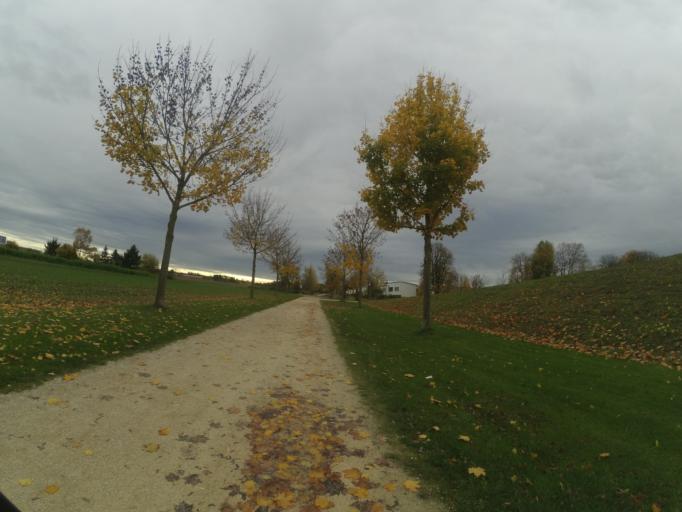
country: DE
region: Bavaria
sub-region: Swabia
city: Neu-Ulm
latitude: 48.3806
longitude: 10.0142
